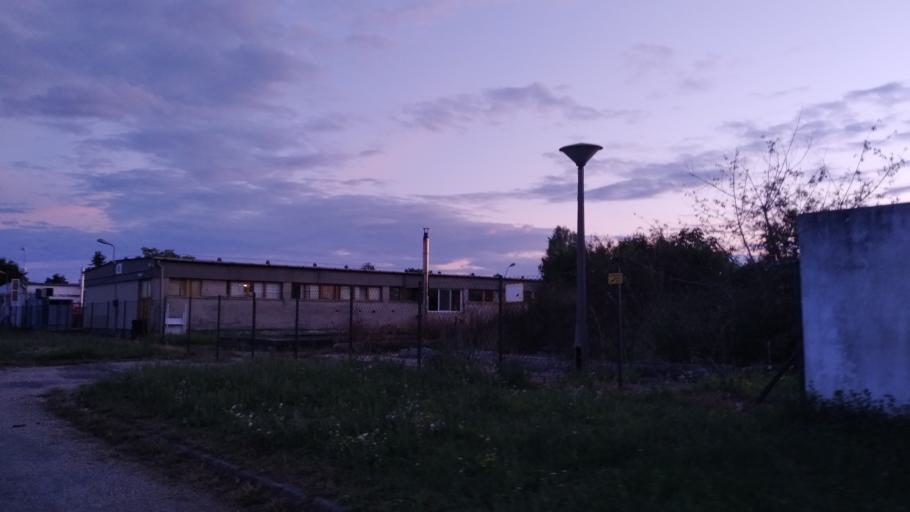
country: HU
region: Pest
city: Budakalasz
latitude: 47.6235
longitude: 19.0641
